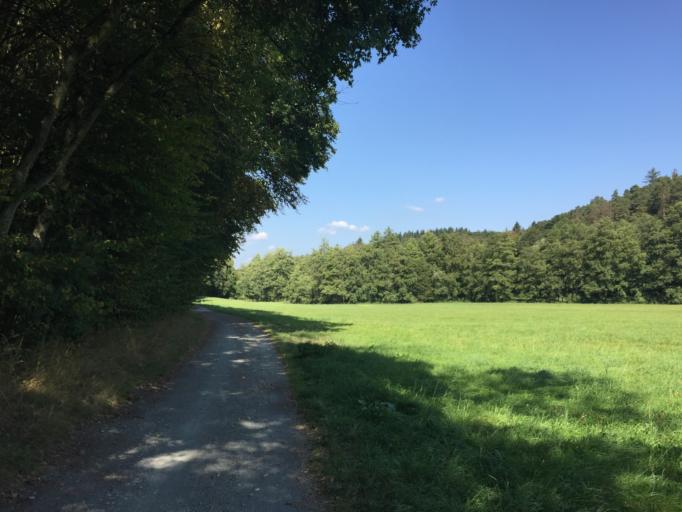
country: DE
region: Hesse
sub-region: Regierungsbezirk Giessen
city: Schwalbach
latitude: 50.4855
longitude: 8.4311
